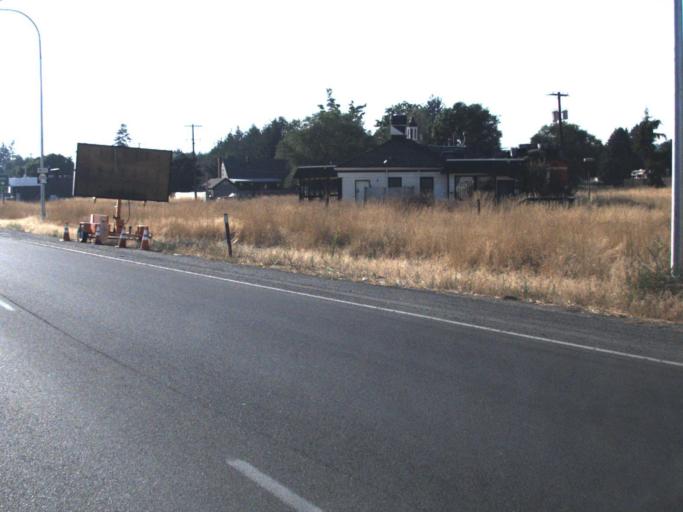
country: US
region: Washington
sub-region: Spokane County
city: Trentwood
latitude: 47.6955
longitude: -117.2001
